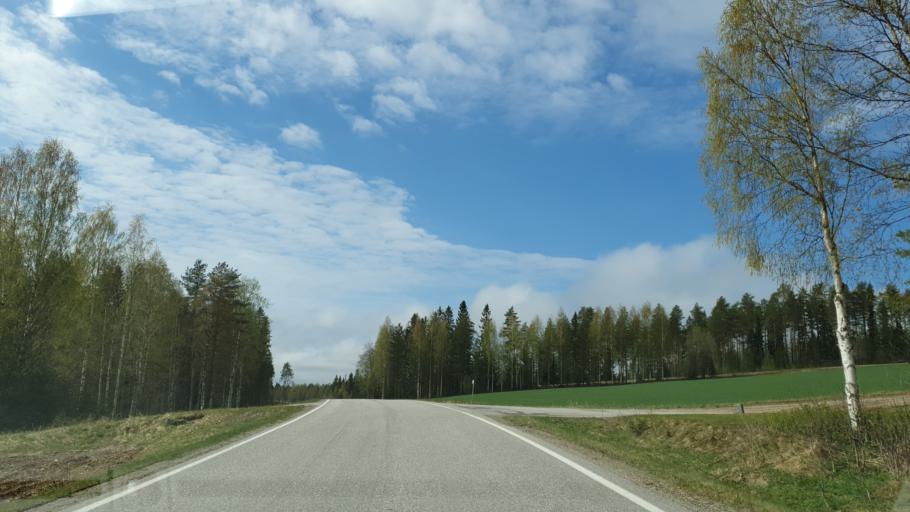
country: FI
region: Kainuu
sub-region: Kehys-Kainuu
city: Kuhmo
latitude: 64.1252
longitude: 29.6453
